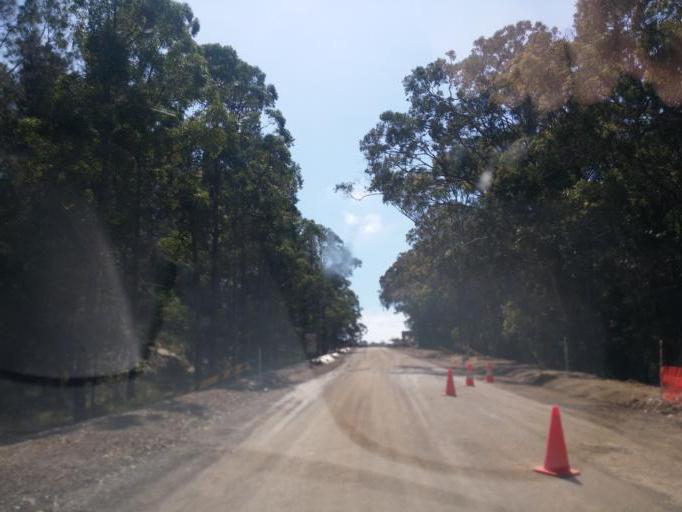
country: AU
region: New South Wales
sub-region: Great Lakes
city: Forster
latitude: -32.3891
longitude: 152.4430
